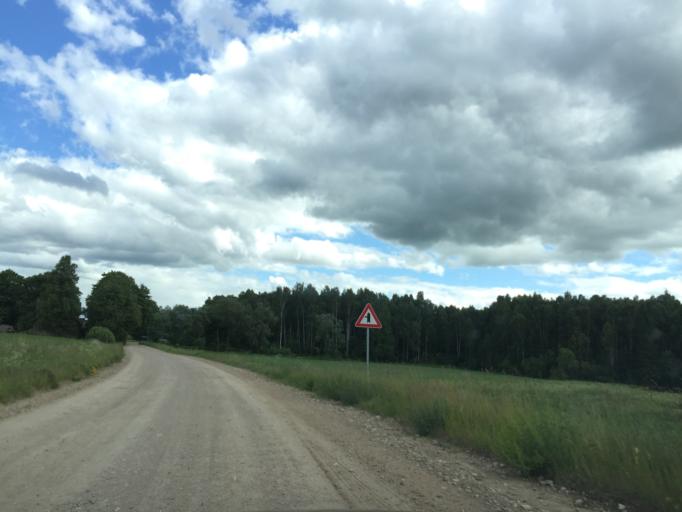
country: LV
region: Vecumnieki
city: Vecumnieki
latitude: 56.4675
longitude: 24.4255
